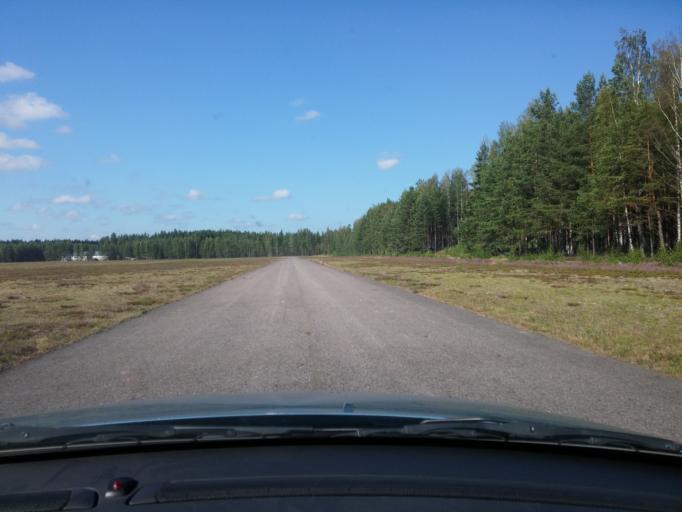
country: FI
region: Uusimaa
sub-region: Helsinki
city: Kaerkoelae
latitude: 60.7430
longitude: 24.0988
